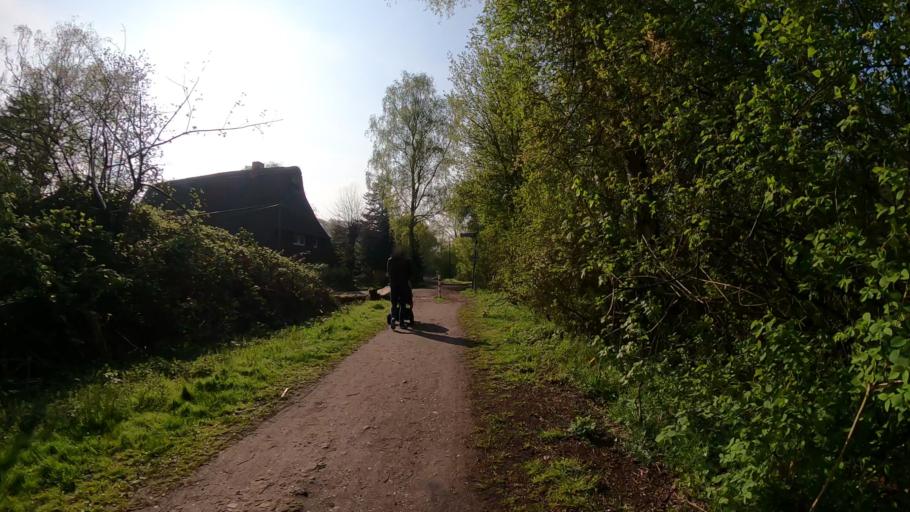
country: DE
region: Hamburg
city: Kleiner Grasbrook
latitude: 53.5074
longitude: 10.0147
